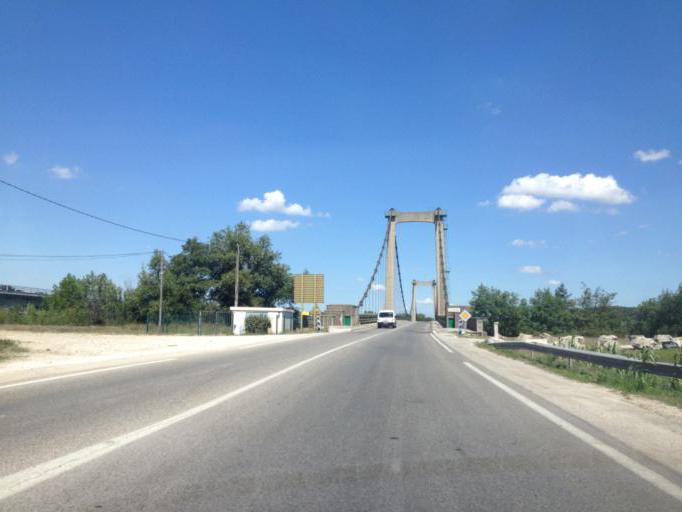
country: FR
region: Languedoc-Roussillon
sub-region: Departement du Gard
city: Montfaucon
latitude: 44.0695
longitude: 4.7676
